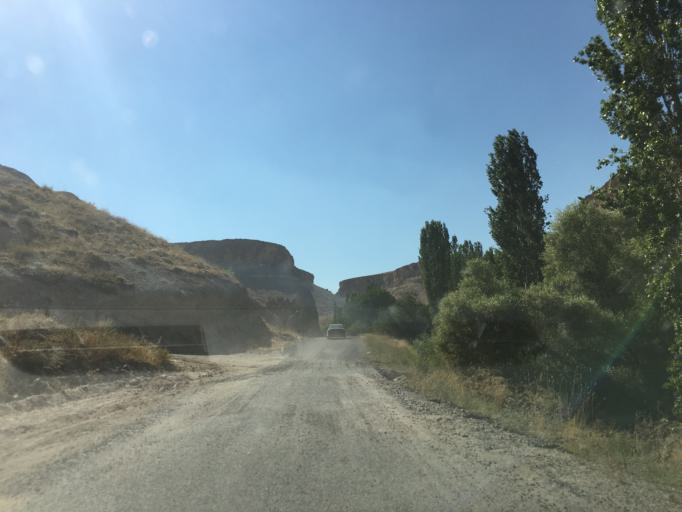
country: TR
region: Kayseri
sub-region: Yesilhisar
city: Yesilhisar
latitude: 38.3447
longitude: 34.9682
